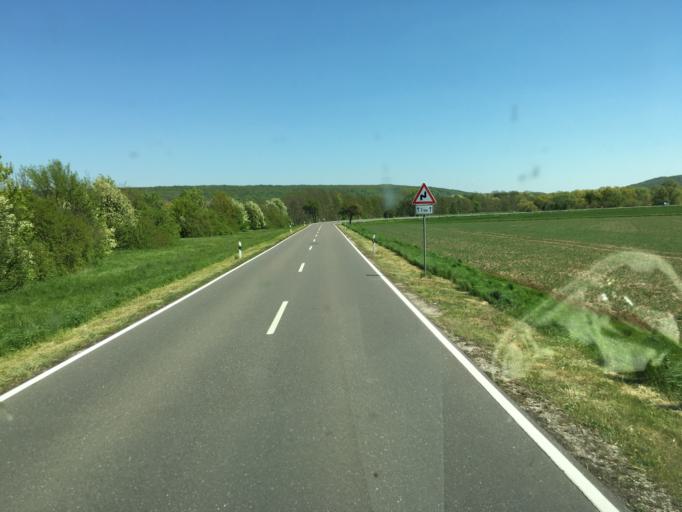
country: DE
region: Thuringia
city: Rossleben
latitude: 51.2736
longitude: 11.4699
